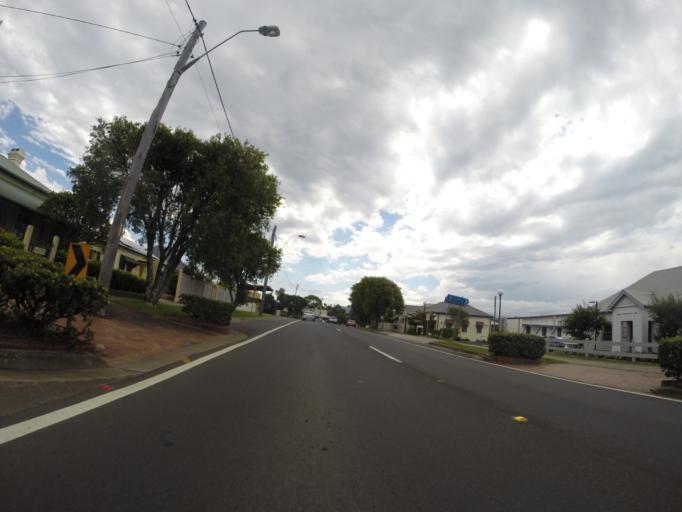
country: AU
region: New South Wales
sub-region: Shoalhaven Shire
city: Milton
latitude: -35.3178
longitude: 150.4397
